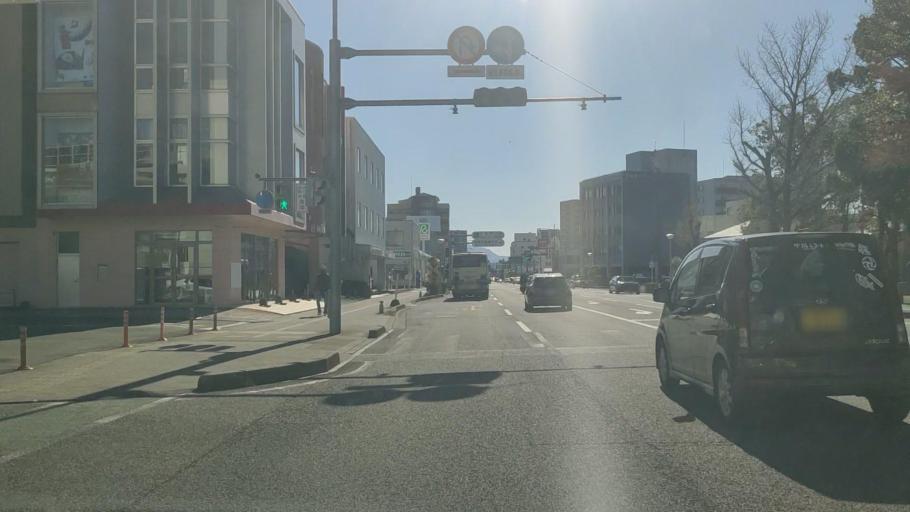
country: JP
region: Miyazaki
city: Miyazaki-shi
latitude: 31.9120
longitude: 131.4298
